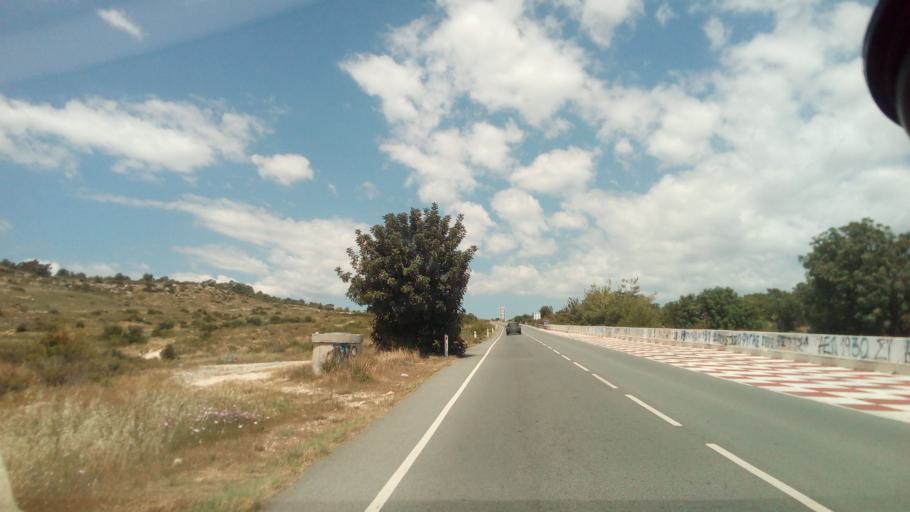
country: CY
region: Limassol
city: Sotira
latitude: 34.7093
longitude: 32.8923
